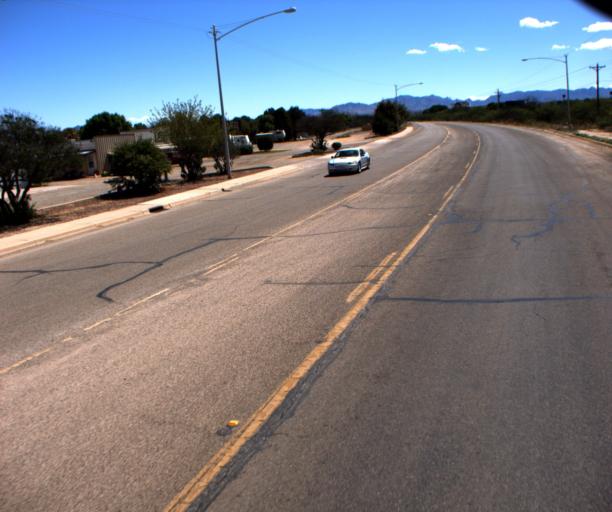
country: US
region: Arizona
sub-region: Cochise County
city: Benson
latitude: 31.9652
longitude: -110.2842
